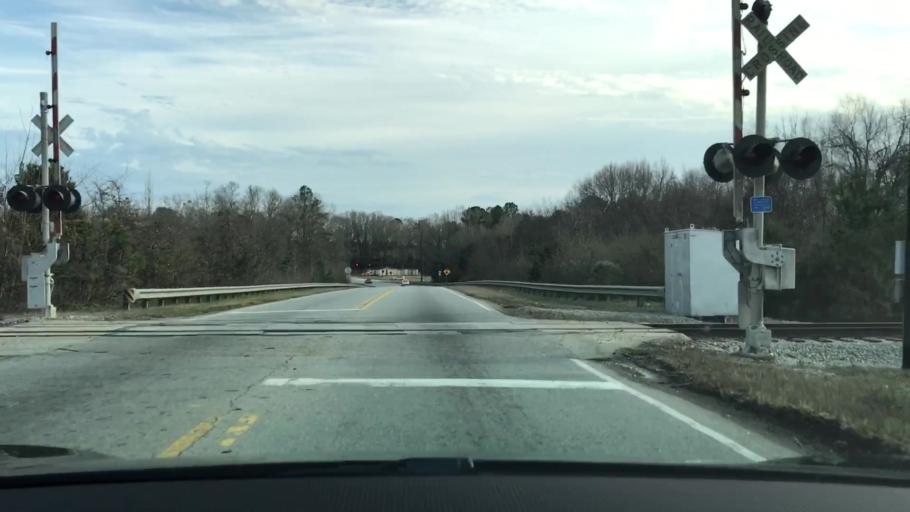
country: US
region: Georgia
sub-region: Warren County
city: West Warrenton
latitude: 33.4054
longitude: -82.6716
